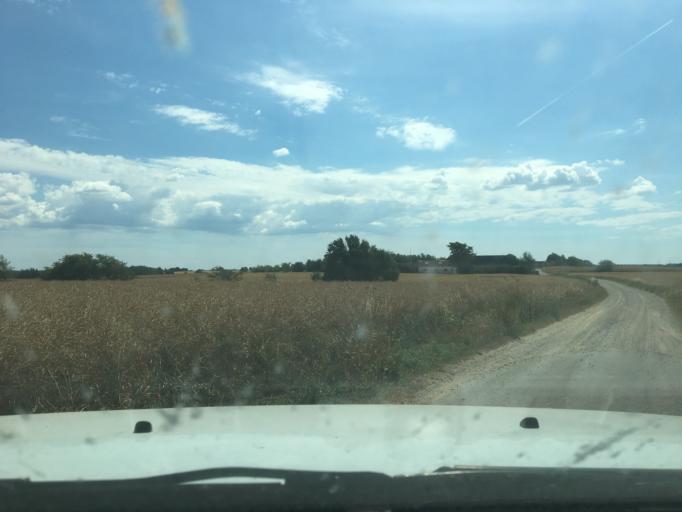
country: DK
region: Central Jutland
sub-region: Randers Kommune
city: Assentoft
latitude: 56.3502
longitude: 10.1863
